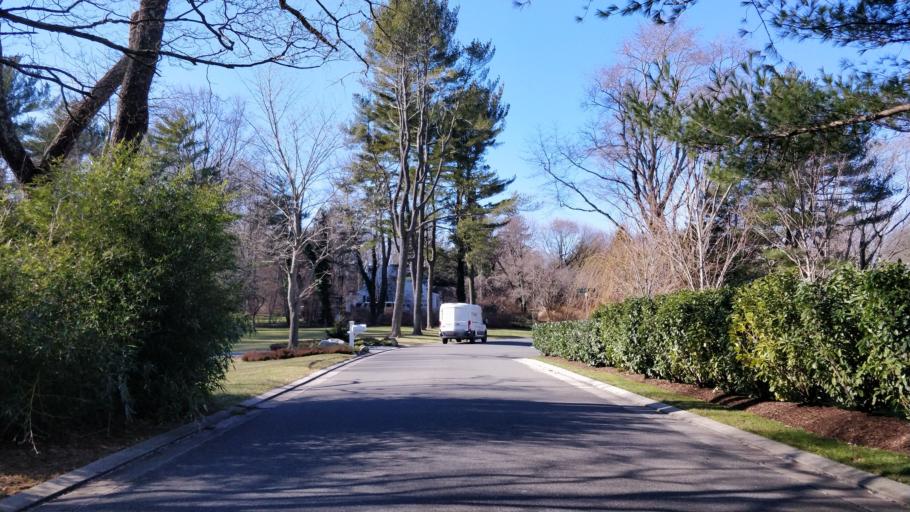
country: US
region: New York
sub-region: Nassau County
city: Glen Head
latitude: 40.8266
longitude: -73.6190
